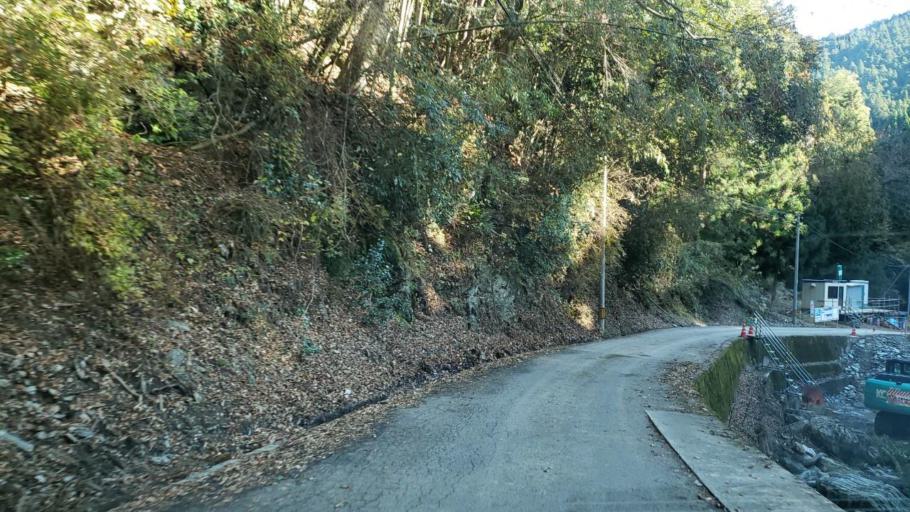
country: JP
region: Tokushima
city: Ikedacho
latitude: 33.9890
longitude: 133.9829
